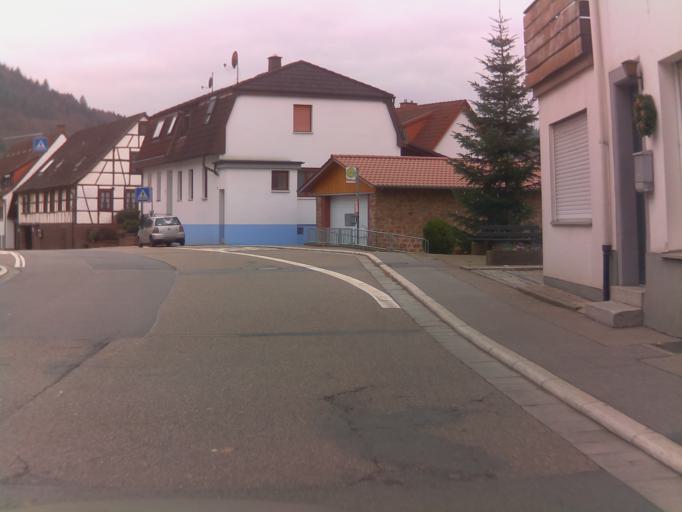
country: DE
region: Baden-Wuerttemberg
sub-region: Karlsruhe Region
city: Eberbach
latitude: 49.4543
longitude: 8.9540
